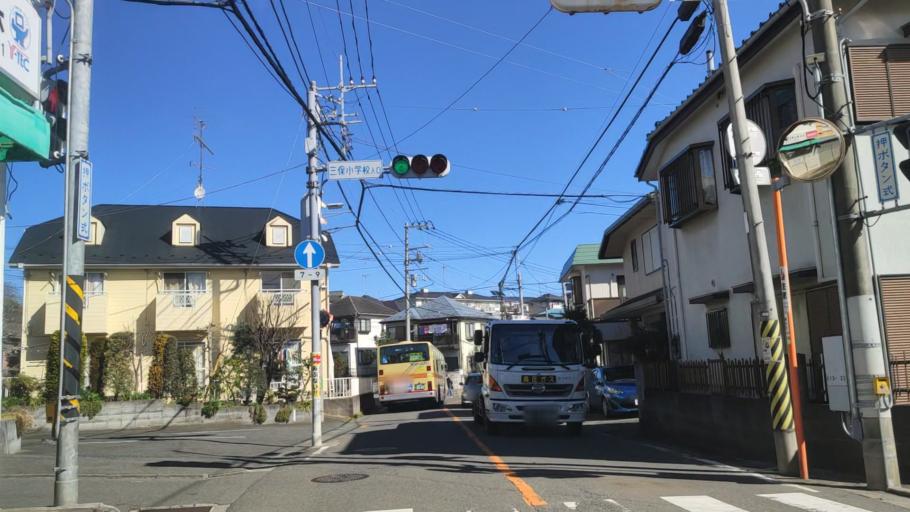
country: JP
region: Tokyo
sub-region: Machida-shi
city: Machida
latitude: 35.5151
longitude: 139.5296
